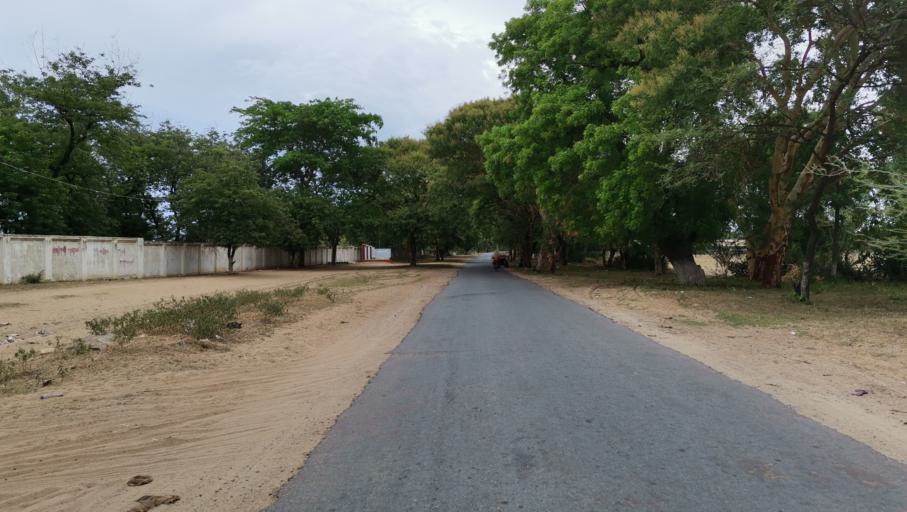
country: MM
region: Mandalay
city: Myingyan
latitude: 21.8473
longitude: 95.4294
